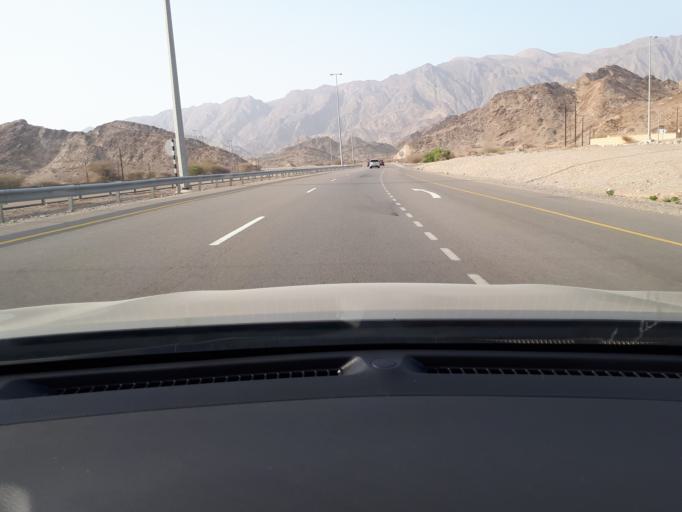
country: OM
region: Muhafazat Masqat
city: Muscat
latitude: 23.3110
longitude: 58.7296
